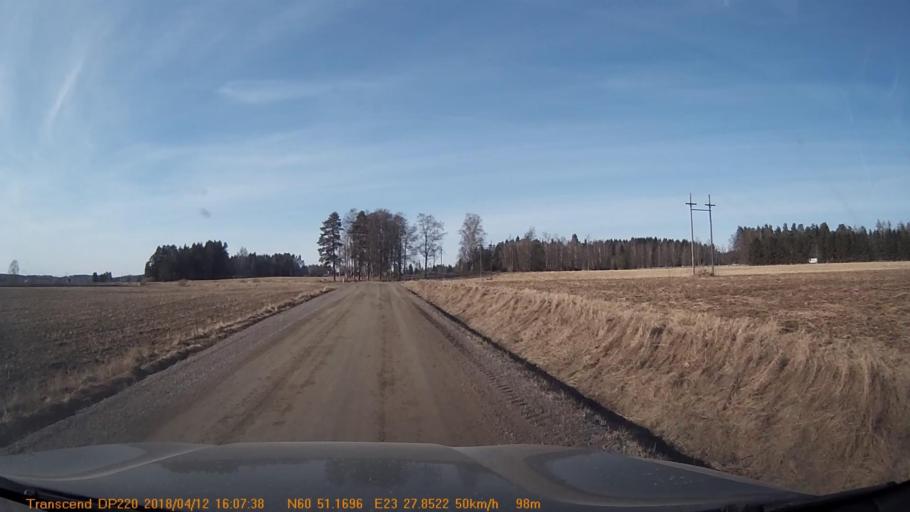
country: FI
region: Haeme
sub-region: Forssa
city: Jokioinen
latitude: 60.8529
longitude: 23.4641
